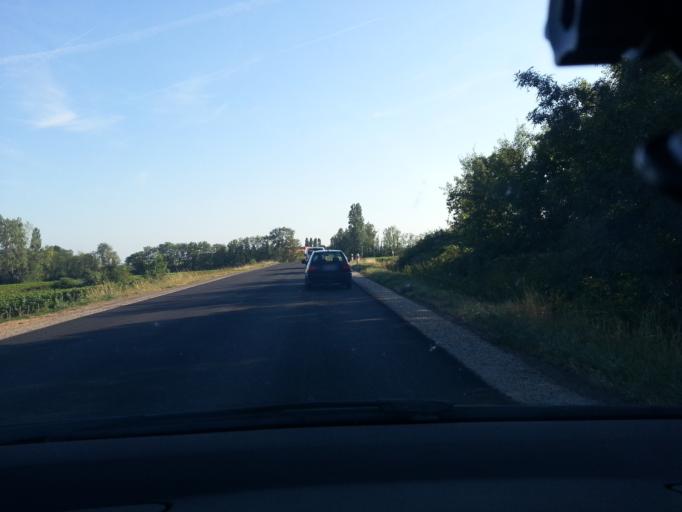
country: FR
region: Bourgogne
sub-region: Departement de la Cote-d'Or
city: Meursault
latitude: 46.9872
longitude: 4.7923
